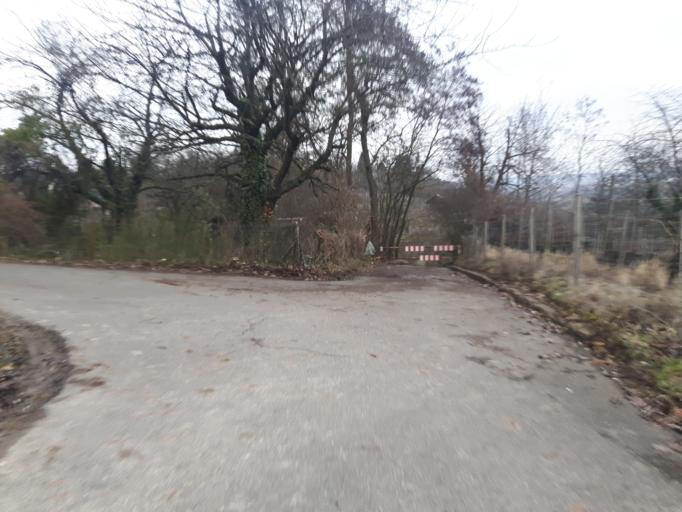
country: DE
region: Baden-Wuerttemberg
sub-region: Regierungsbezirk Stuttgart
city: Nordheim
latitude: 49.1230
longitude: 9.1686
